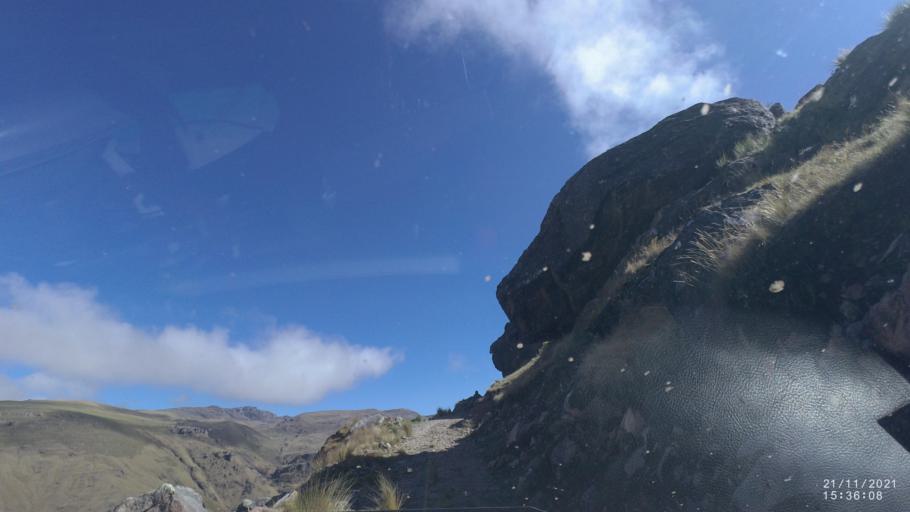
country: BO
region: Cochabamba
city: Cochabamba
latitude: -16.9606
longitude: -66.2664
